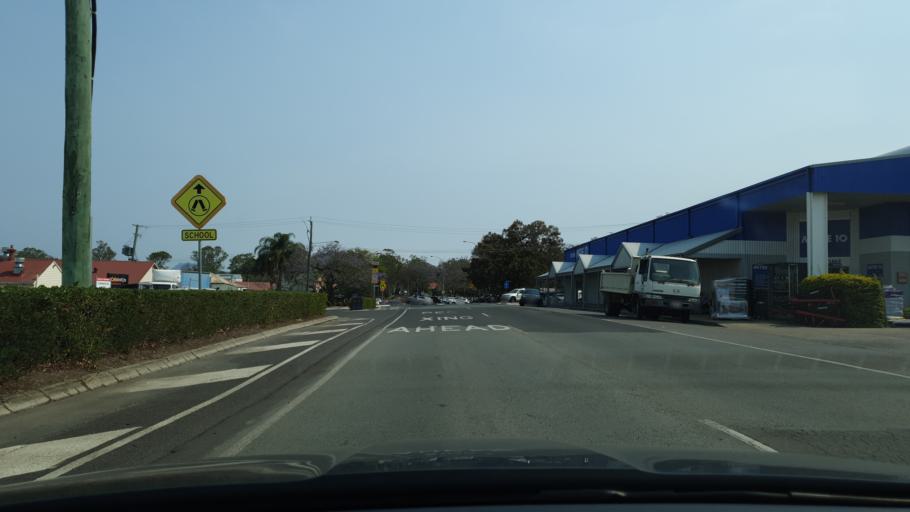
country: AU
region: Queensland
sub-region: Ipswich
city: Deebing Heights
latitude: -27.9964
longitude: 152.6816
